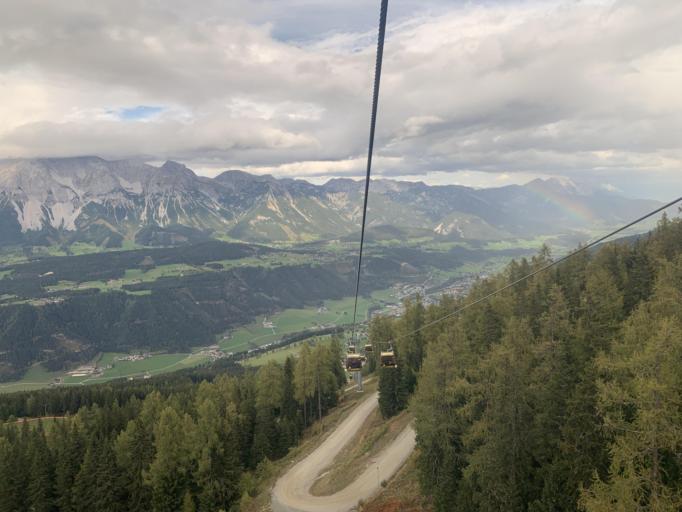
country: AT
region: Styria
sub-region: Politischer Bezirk Liezen
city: Schladming
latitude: 47.3624
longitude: 13.6412
